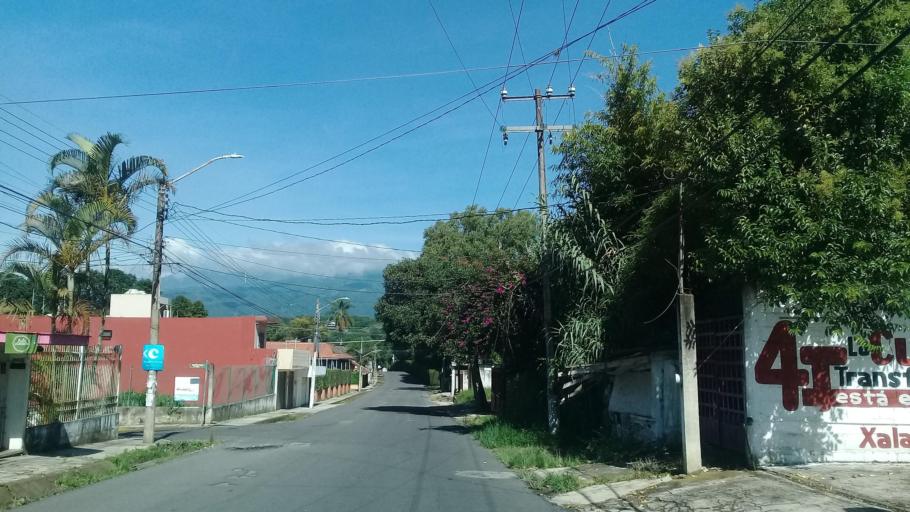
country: MX
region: Veracruz
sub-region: Xalapa
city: Xalapa de Enriquez
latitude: 19.5281
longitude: -96.9444
